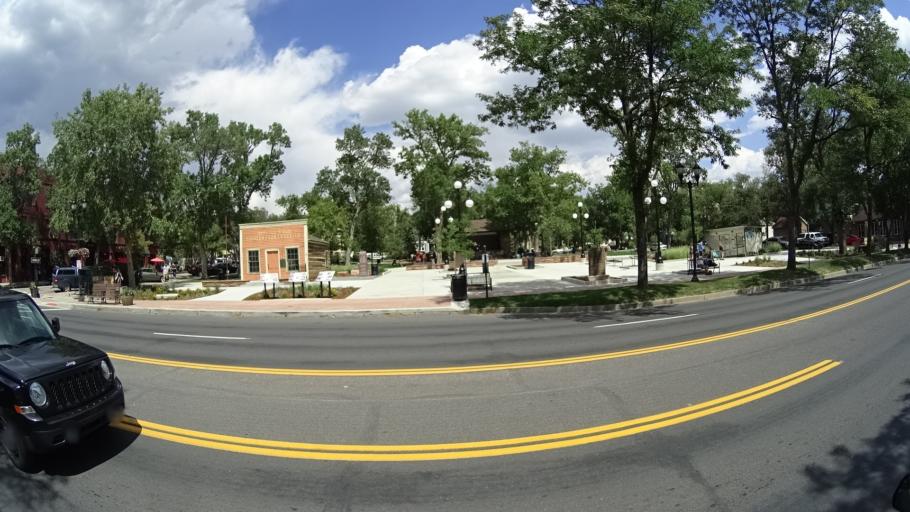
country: US
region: Colorado
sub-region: El Paso County
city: Colorado Springs
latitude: 38.8468
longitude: -104.8613
